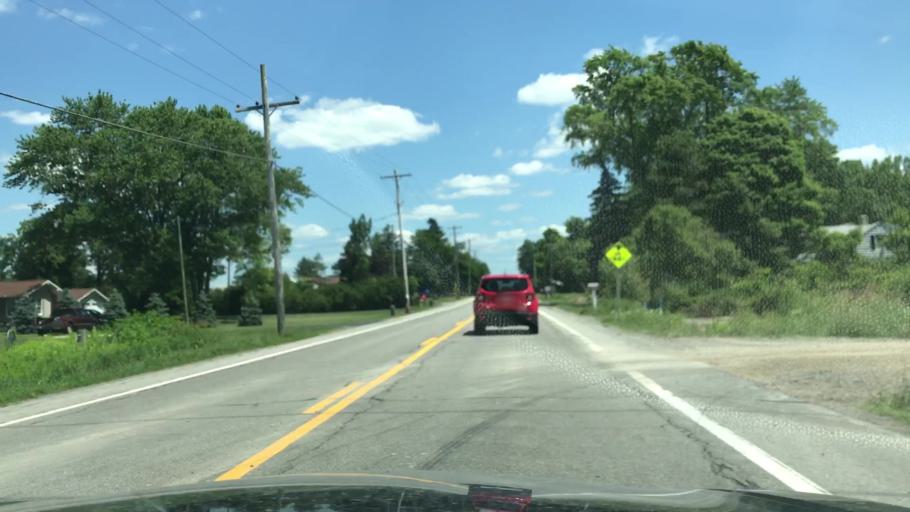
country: US
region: New York
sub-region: Erie County
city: East Aurora
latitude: 42.7674
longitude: -78.5683
